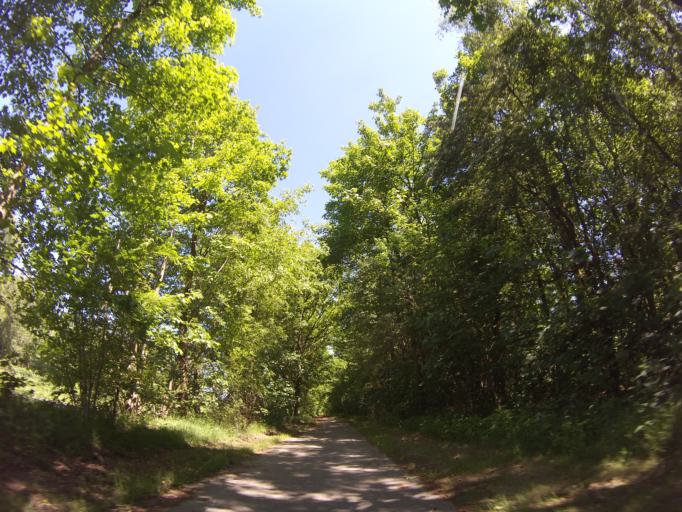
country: NL
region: Drenthe
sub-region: Gemeente Hoogeveen
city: Hoogeveen
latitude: 52.7943
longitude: 6.5149
